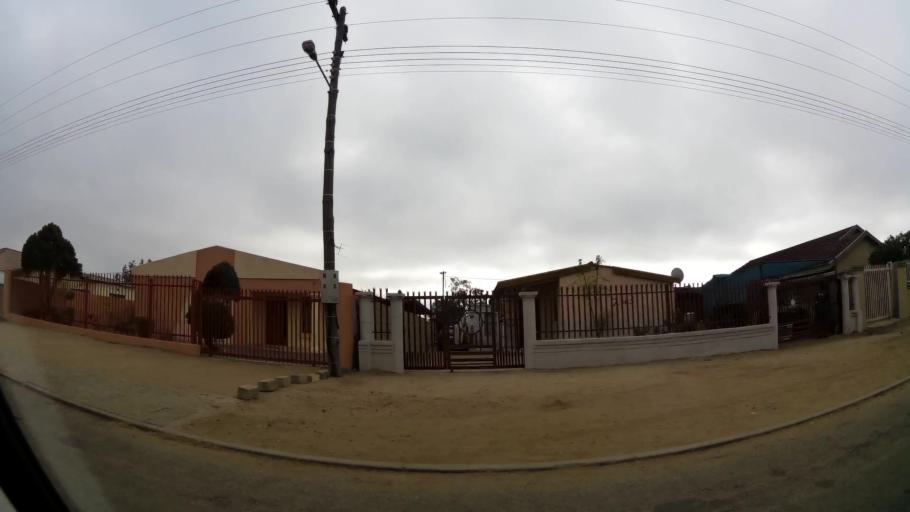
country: ZA
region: Limpopo
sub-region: Capricorn District Municipality
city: Polokwane
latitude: -23.8366
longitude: 29.3846
